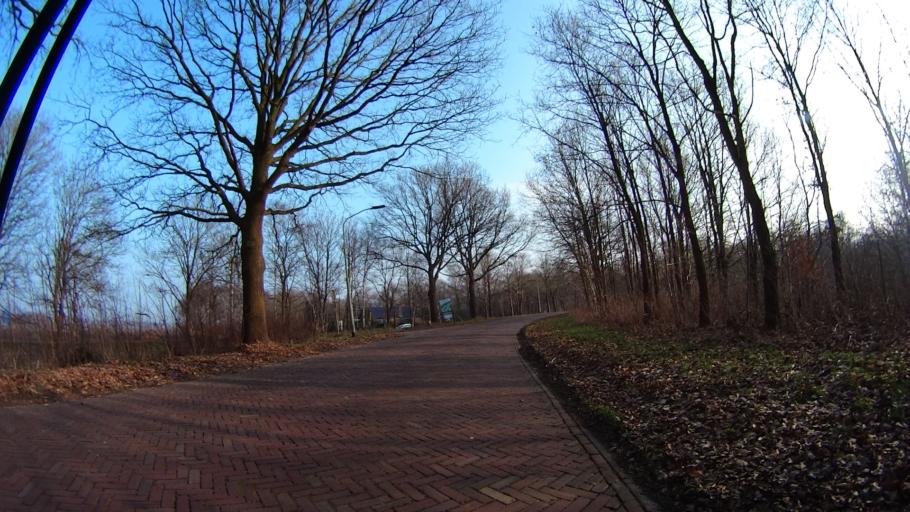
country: NL
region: Drenthe
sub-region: Gemeente Emmen
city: Emmen
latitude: 52.8001
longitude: 6.9483
